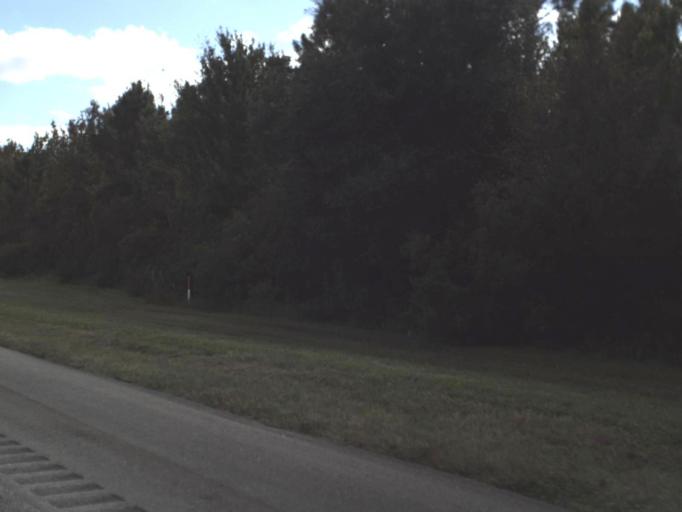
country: US
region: Florida
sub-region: Indian River County
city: Fellsmere
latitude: 27.6193
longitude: -80.8360
